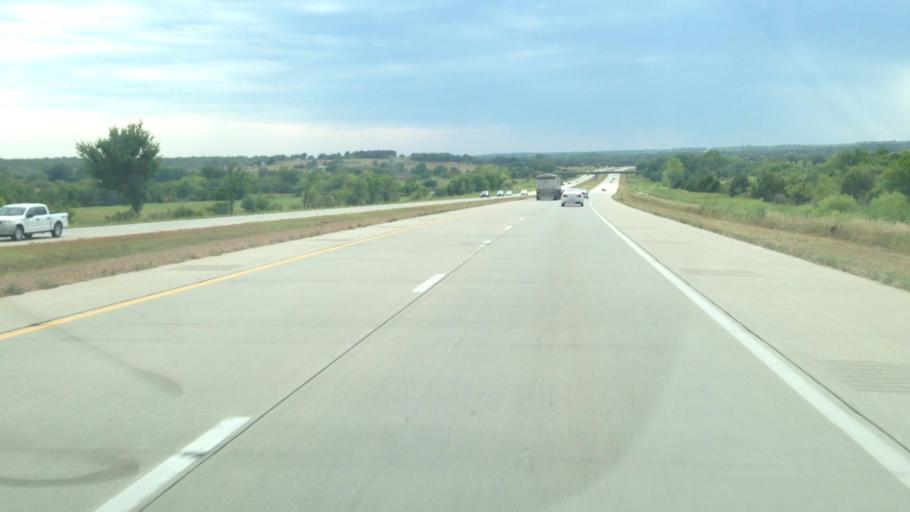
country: US
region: Kansas
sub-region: Franklin County
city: Ottawa
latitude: 38.5621
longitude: -95.3142
